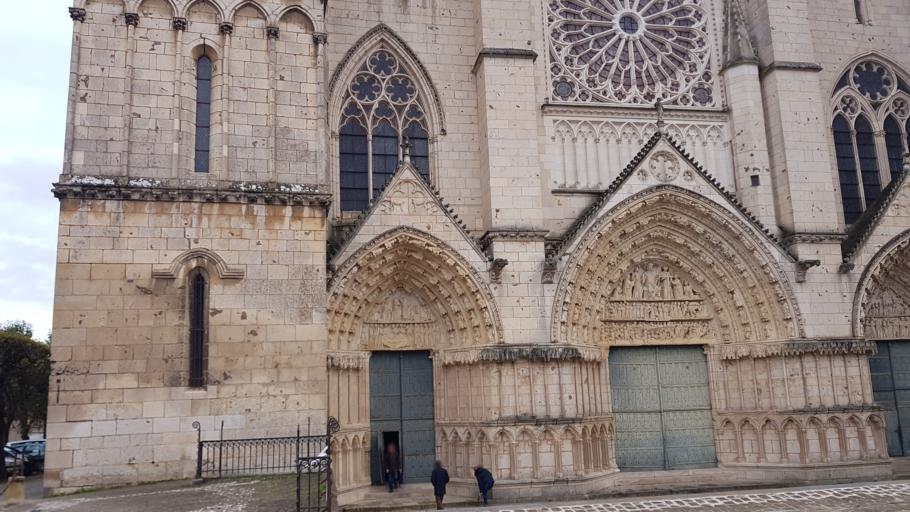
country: FR
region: Poitou-Charentes
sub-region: Departement de la Vienne
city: Poitiers
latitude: 46.5808
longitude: 0.3486
